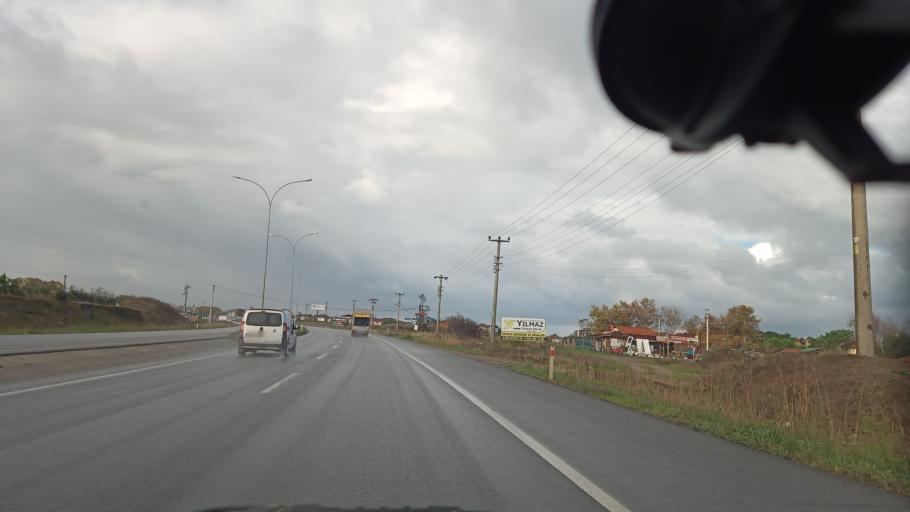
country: TR
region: Sakarya
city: Karasu
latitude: 41.0868
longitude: 30.7510
